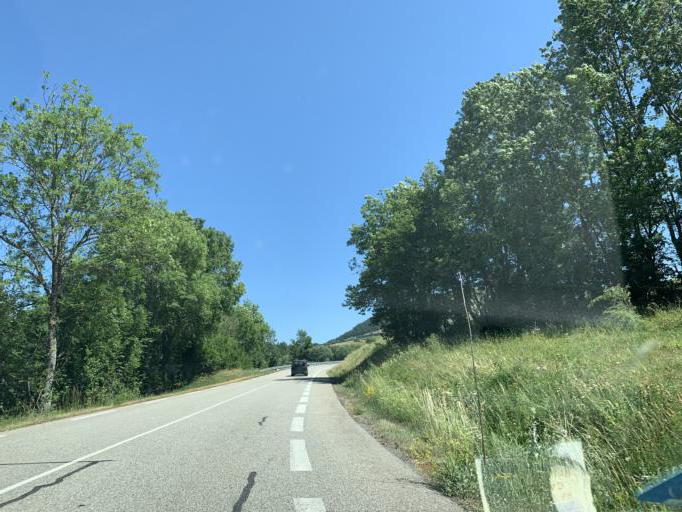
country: FR
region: Provence-Alpes-Cote d'Azur
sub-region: Departement des Hautes-Alpes
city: Saint-Bonnet-en-Champsaur
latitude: 44.6315
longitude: 6.1367
